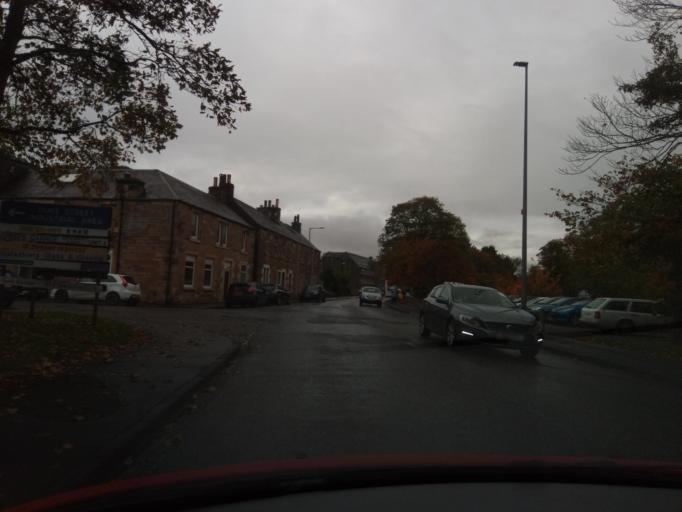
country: GB
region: Scotland
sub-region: The Scottish Borders
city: Galashiels
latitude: 55.6221
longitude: -2.8205
